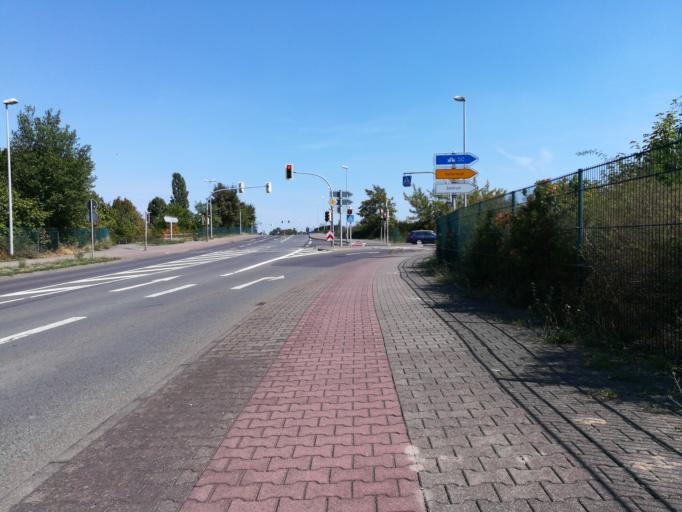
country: DE
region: Saxony-Anhalt
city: Neue Neustadt
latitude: 52.1517
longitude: 11.6247
